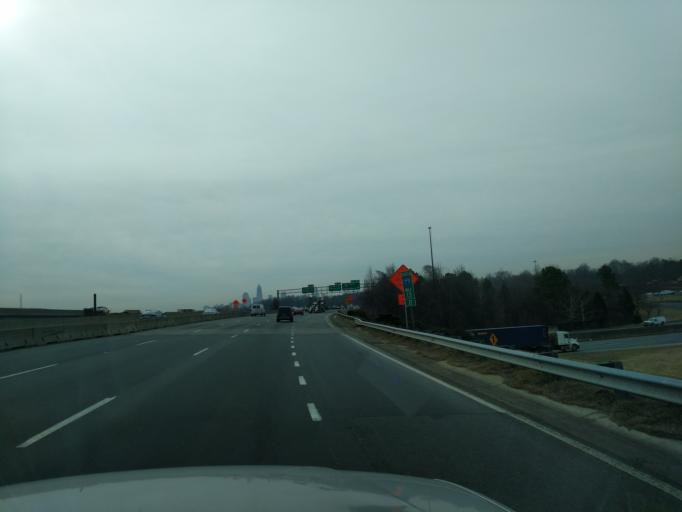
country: US
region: North Carolina
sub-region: Mecklenburg County
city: Charlotte
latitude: 35.2741
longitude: -80.8447
